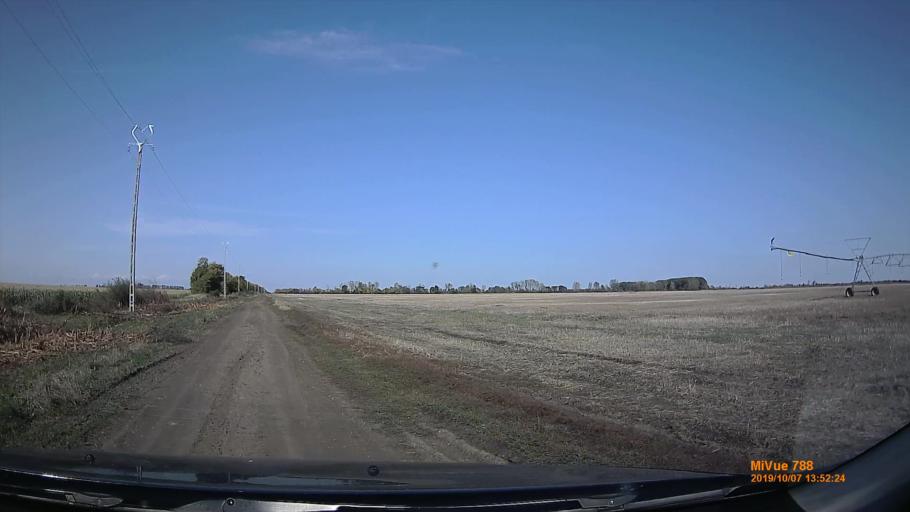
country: HU
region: Jasz-Nagykun-Szolnok
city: Cserkeszolo
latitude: 46.8855
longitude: 20.2142
